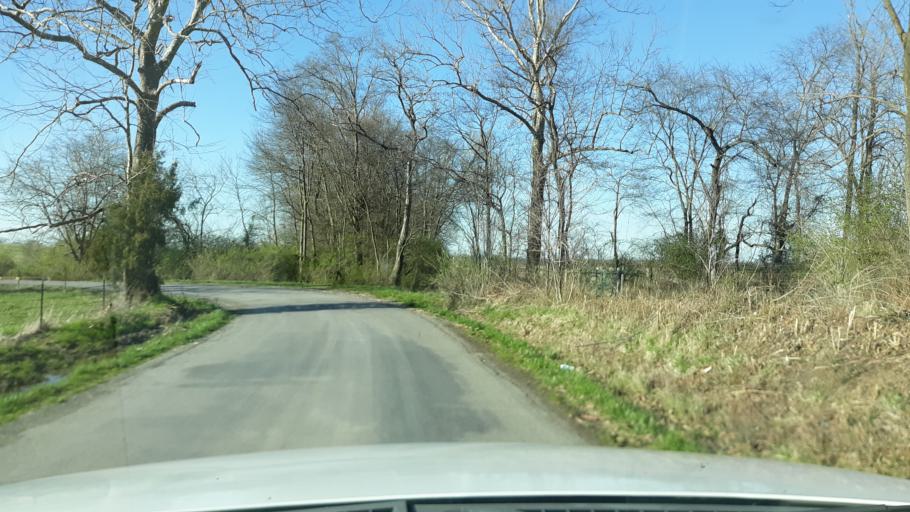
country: US
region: Illinois
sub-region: Saline County
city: Harrisburg
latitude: 37.7640
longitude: -88.5818
